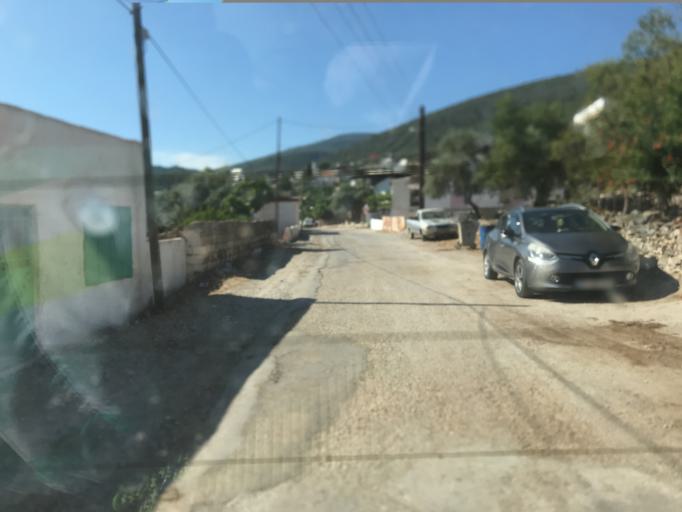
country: TR
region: Mugla
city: Kiulukioi
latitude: 37.3688
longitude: 27.4942
